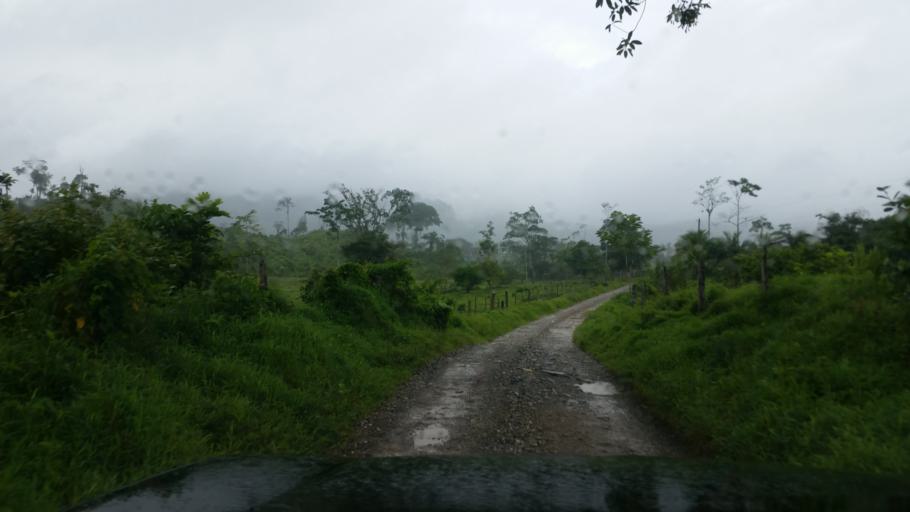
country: NI
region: Atlantico Norte (RAAN)
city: Bonanza
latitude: 14.0855
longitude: -84.6771
